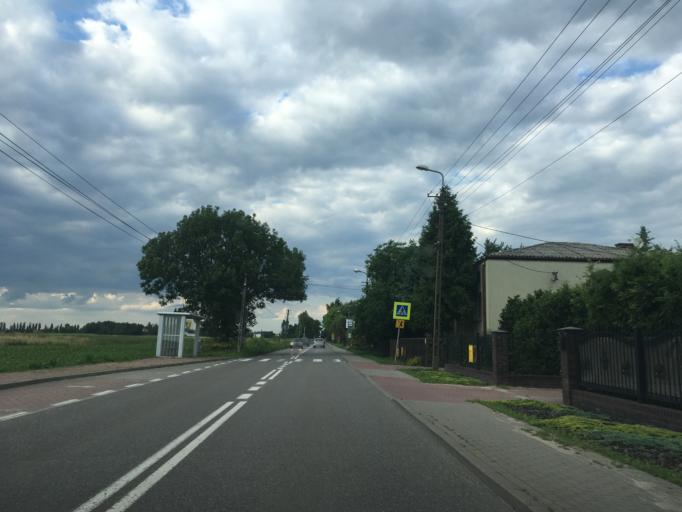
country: PL
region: Masovian Voivodeship
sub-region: Powiat piaseczynski
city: Lesznowola
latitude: 52.0961
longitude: 20.9735
